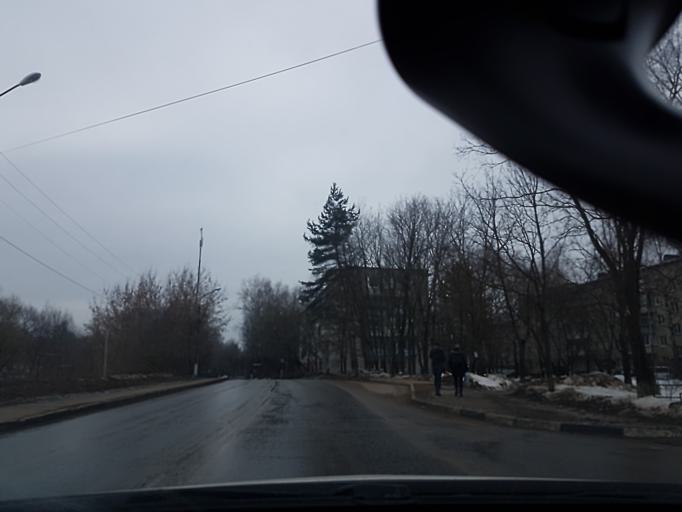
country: RU
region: Moskovskaya
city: Istra
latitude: 55.9071
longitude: 36.8679
